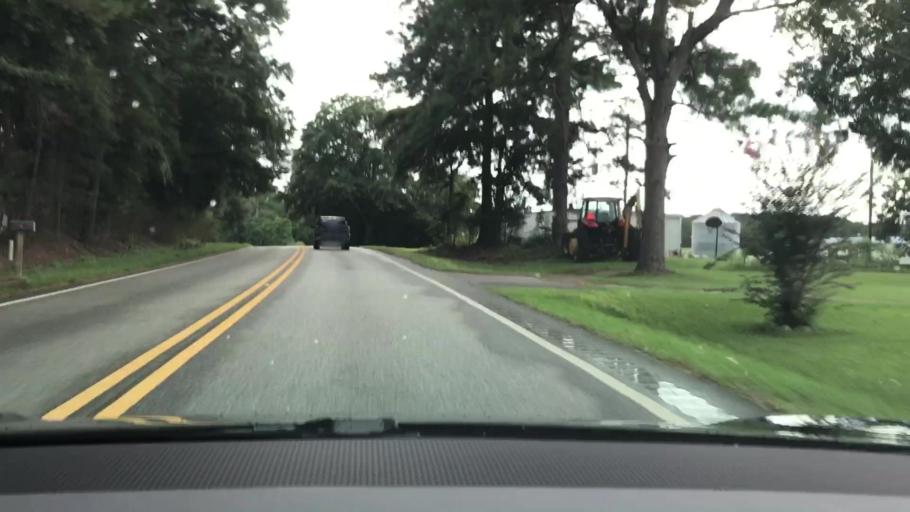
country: US
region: Alabama
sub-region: Geneva County
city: Samson
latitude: 31.0011
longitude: -86.1318
